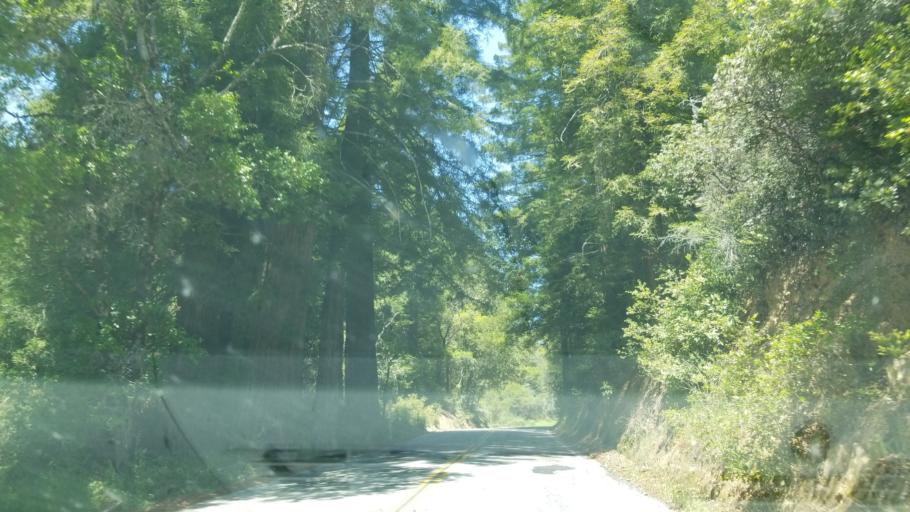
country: US
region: California
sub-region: Santa Cruz County
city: Interlaken
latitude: 37.0097
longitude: -121.7107
